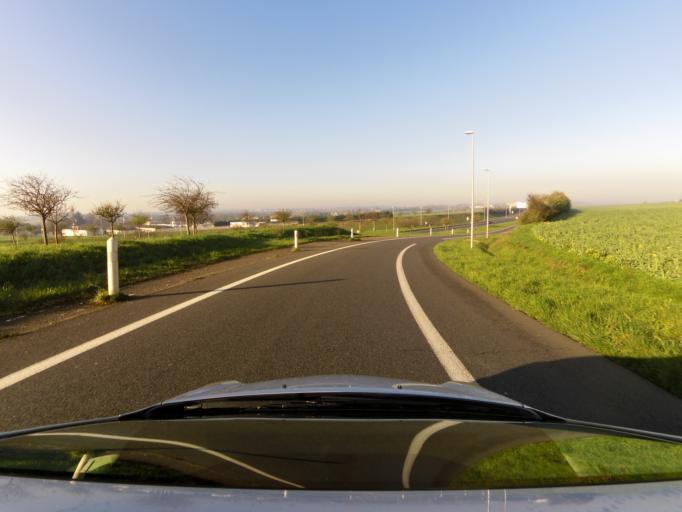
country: FR
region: Lower Normandy
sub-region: Departement du Calvados
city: Bretteville-sur-Odon
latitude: 49.1656
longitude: -0.4290
